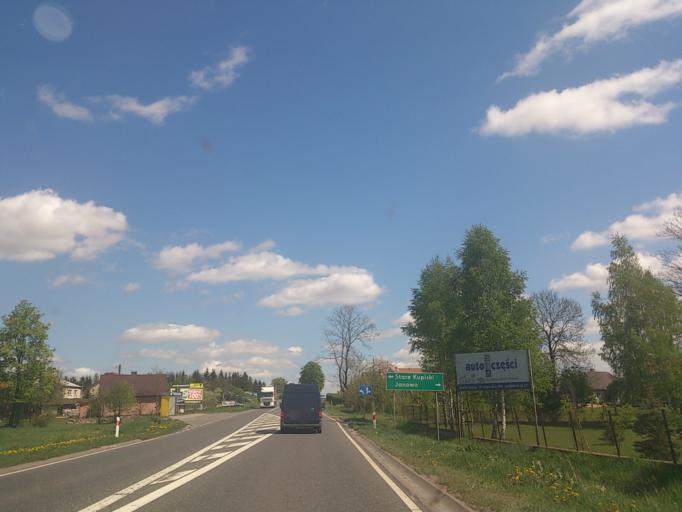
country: PL
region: Podlasie
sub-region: Lomza
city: Lomza
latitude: 53.1686
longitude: 21.9929
